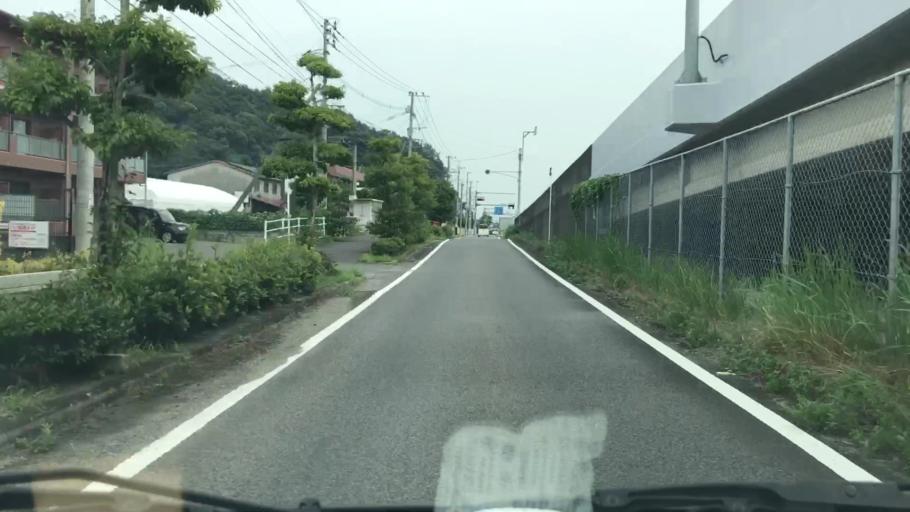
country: JP
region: Saga Prefecture
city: Saga-shi
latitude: 33.2238
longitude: 130.1744
